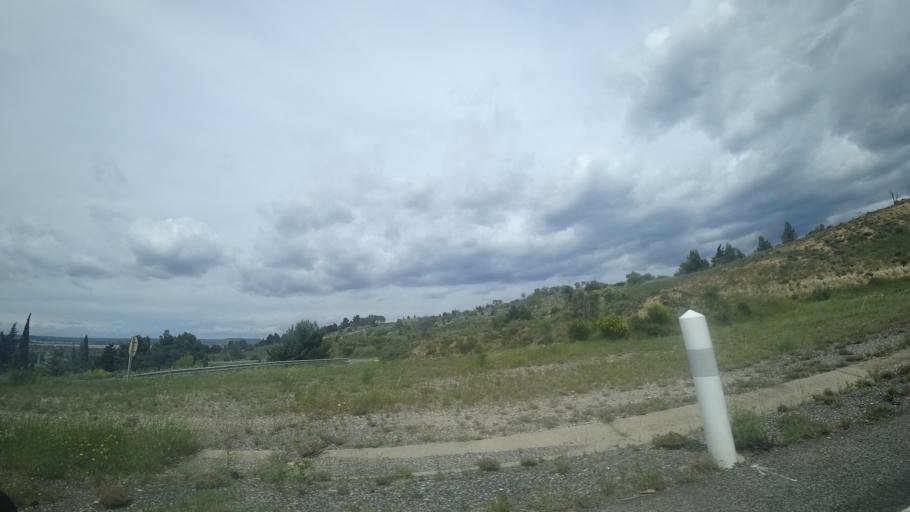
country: FR
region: Languedoc-Roussillon
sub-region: Departement de l'Aude
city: Leucate
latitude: 42.9301
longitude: 3.0156
